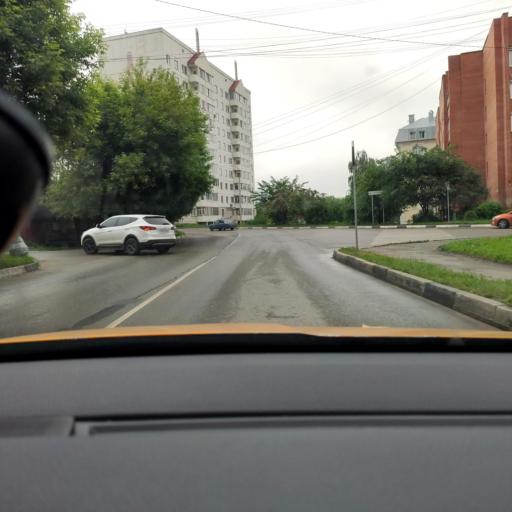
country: RU
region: Moskovskaya
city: Serpukhov
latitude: 54.9074
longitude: 37.4039
